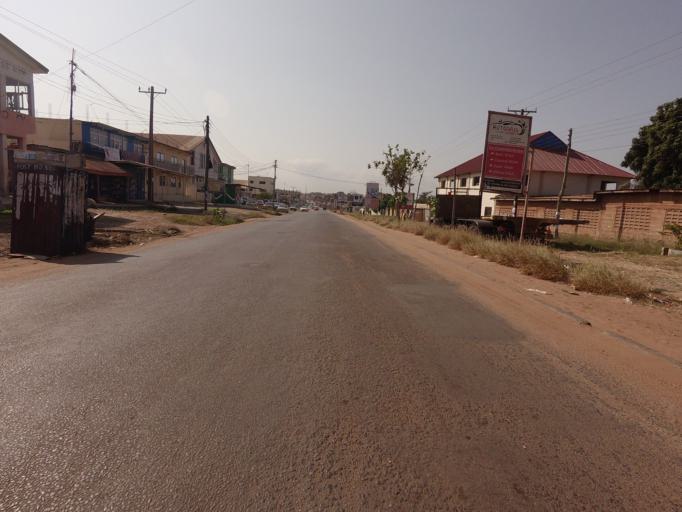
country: GH
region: Greater Accra
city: Teshi Old Town
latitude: 5.5953
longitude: -0.1010
